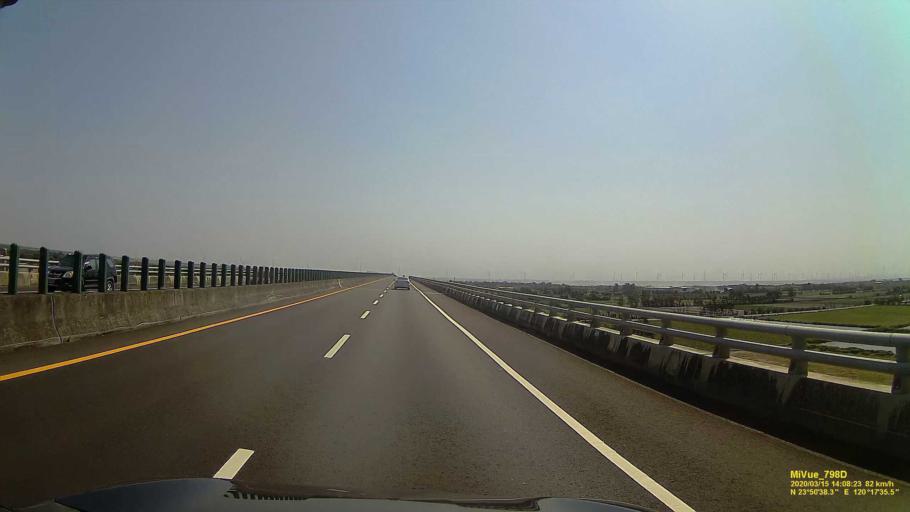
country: TW
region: Taiwan
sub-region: Yunlin
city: Douliu
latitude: 23.8436
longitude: 120.2930
